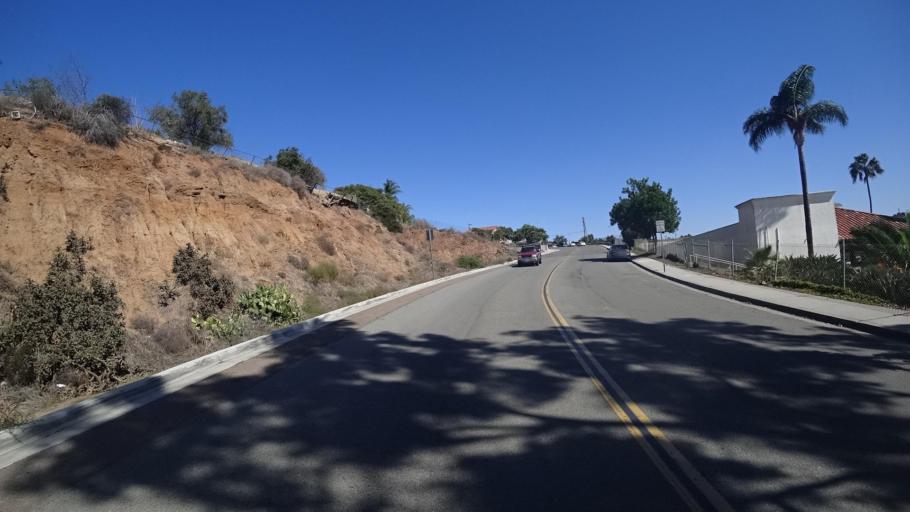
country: US
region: California
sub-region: San Diego County
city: Chula Vista
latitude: 32.6622
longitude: -117.0831
